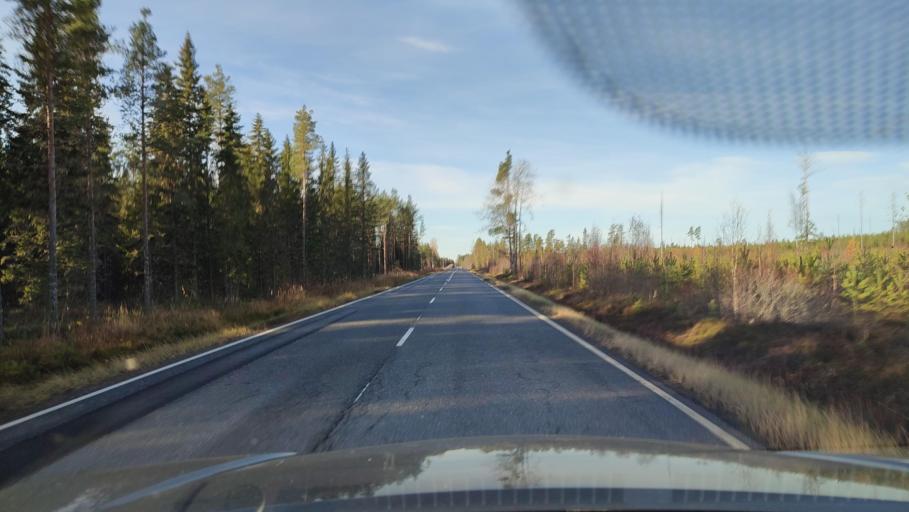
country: FI
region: Ostrobothnia
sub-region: Sydosterbotten
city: Naerpes
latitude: 62.4616
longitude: 21.5353
